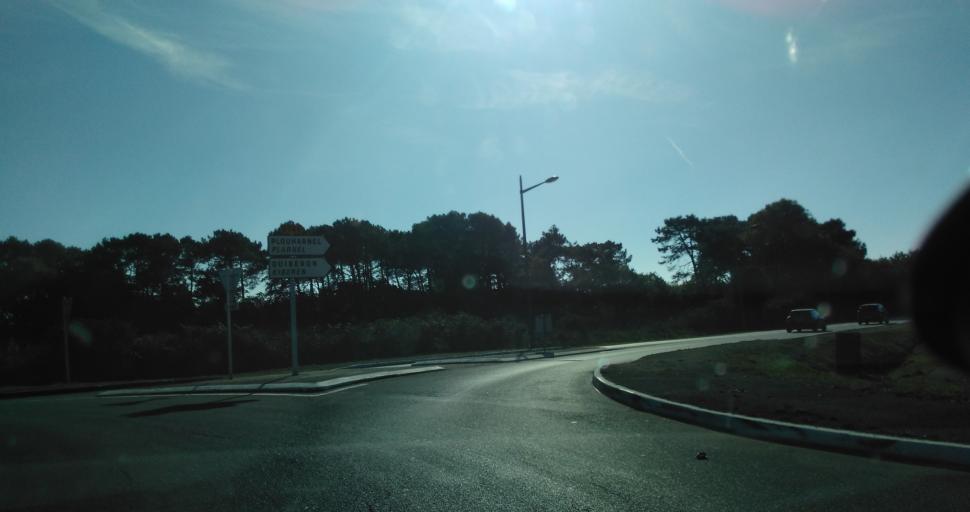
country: FR
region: Brittany
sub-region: Departement du Morbihan
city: Plouharnel
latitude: 47.6109
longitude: -3.0930
